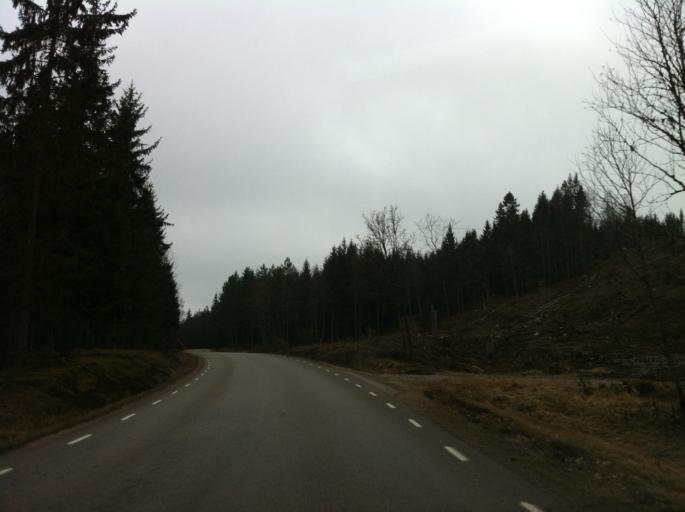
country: SE
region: Vaestra Goetaland
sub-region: Boras Kommun
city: Dalsjofors
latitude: 57.6255
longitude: 13.0973
